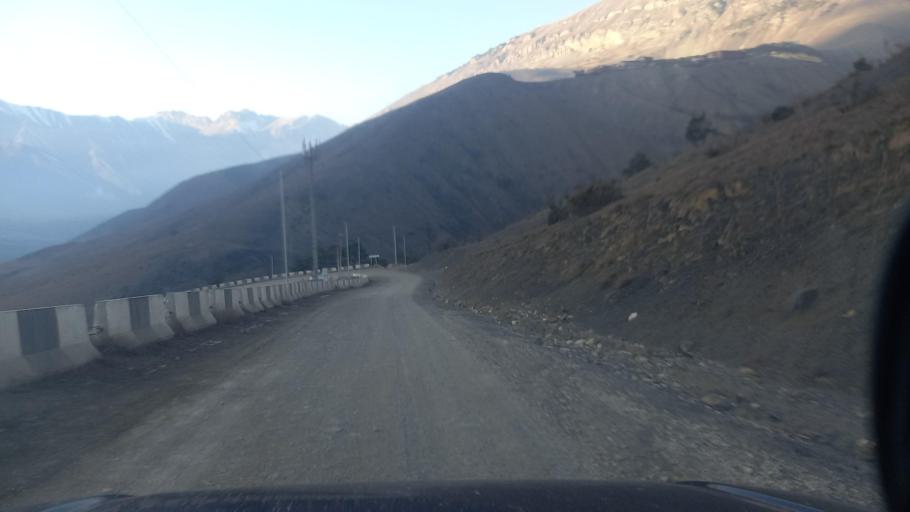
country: RU
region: Ingushetiya
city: Dzhayrakh
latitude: 42.8195
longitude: 44.7038
